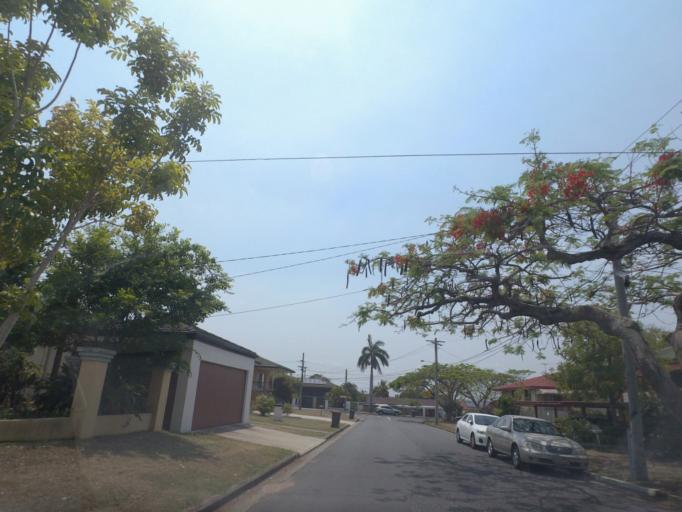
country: AU
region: Queensland
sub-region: Brisbane
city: Nathan
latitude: -27.5631
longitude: 153.0642
